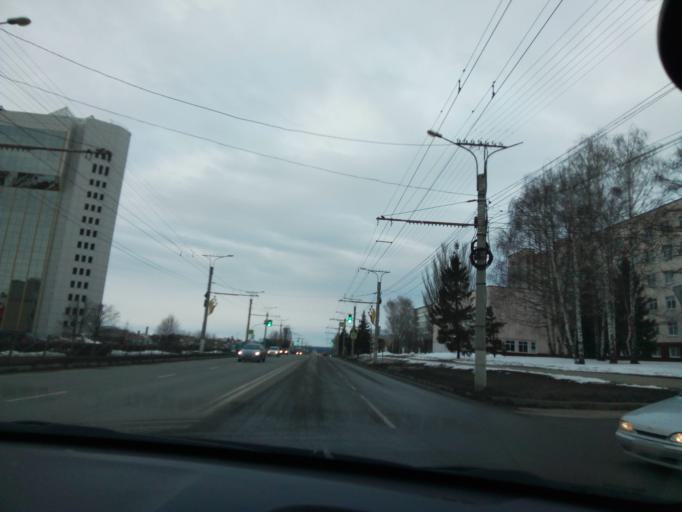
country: RU
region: Chuvashia
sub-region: Cheboksarskiy Rayon
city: Cheboksary
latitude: 56.1385
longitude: 47.2433
